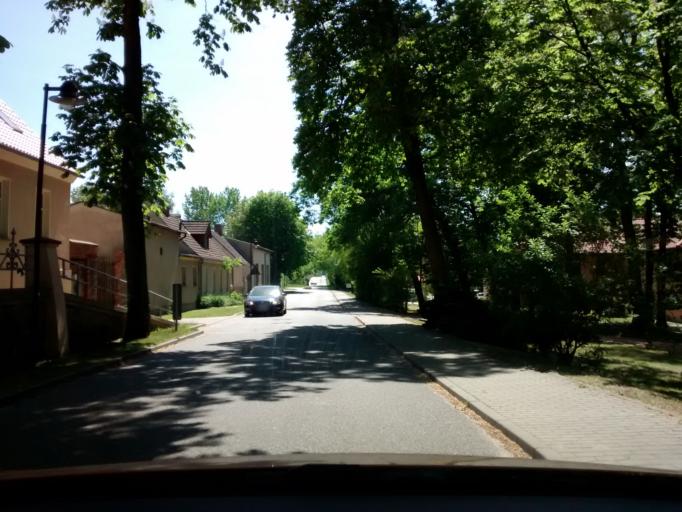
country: DE
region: Brandenburg
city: Reichenwalde
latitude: 52.2635
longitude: 13.9961
